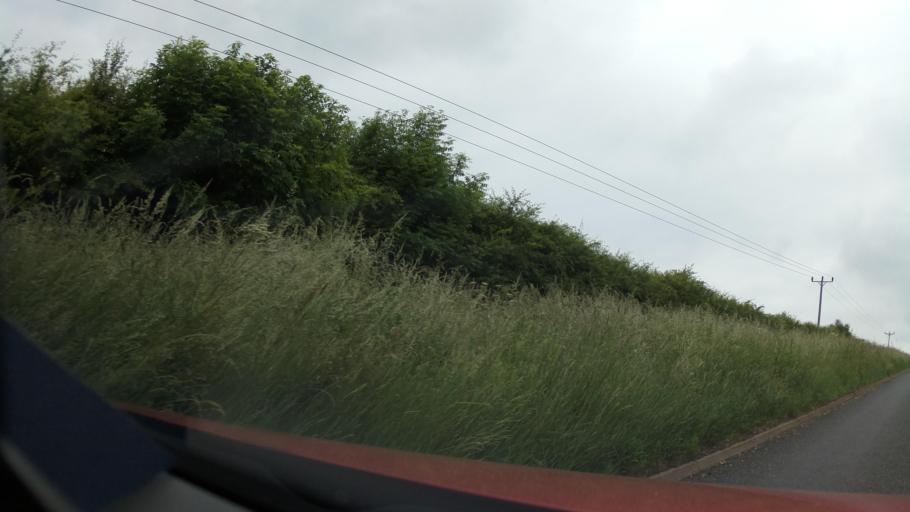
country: GB
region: England
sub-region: District of Rutland
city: Manton
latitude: 52.6277
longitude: -0.7088
